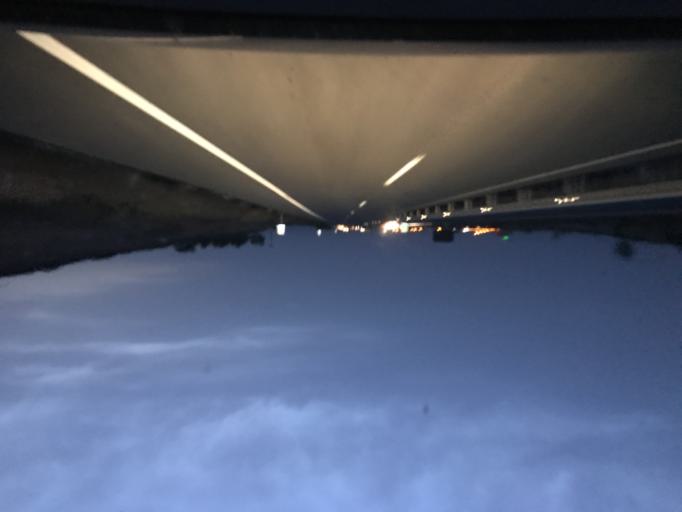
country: ES
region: Andalusia
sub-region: Provincia de Granada
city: Gor
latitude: 37.3920
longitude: -3.0200
